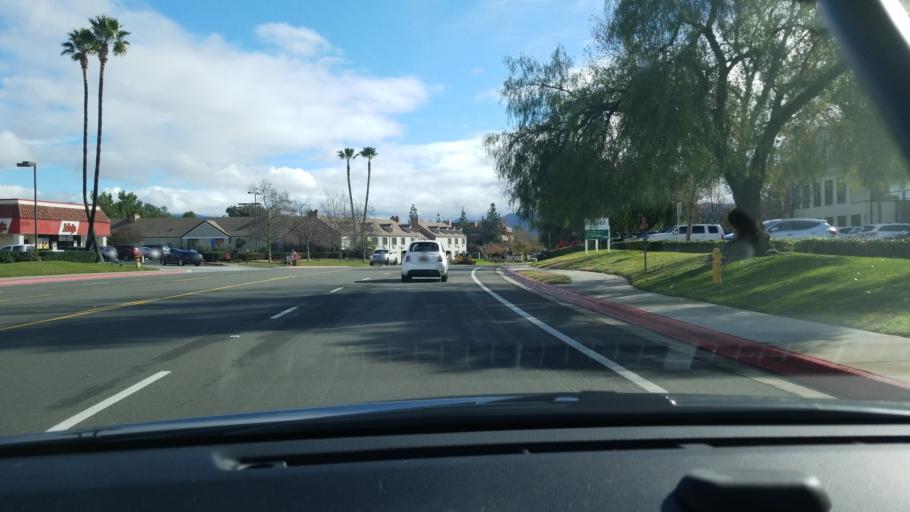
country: US
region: California
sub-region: Riverside County
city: Temecula
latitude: 33.5149
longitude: -117.1597
